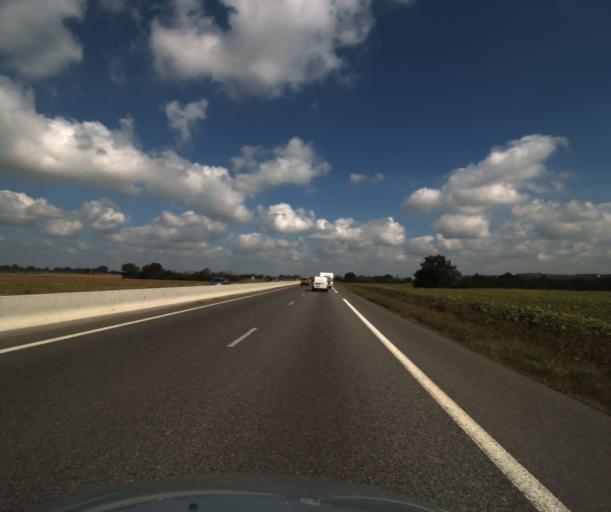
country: FR
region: Midi-Pyrenees
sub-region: Departement de la Haute-Garonne
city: Vernet
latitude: 43.4295
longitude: 1.4185
